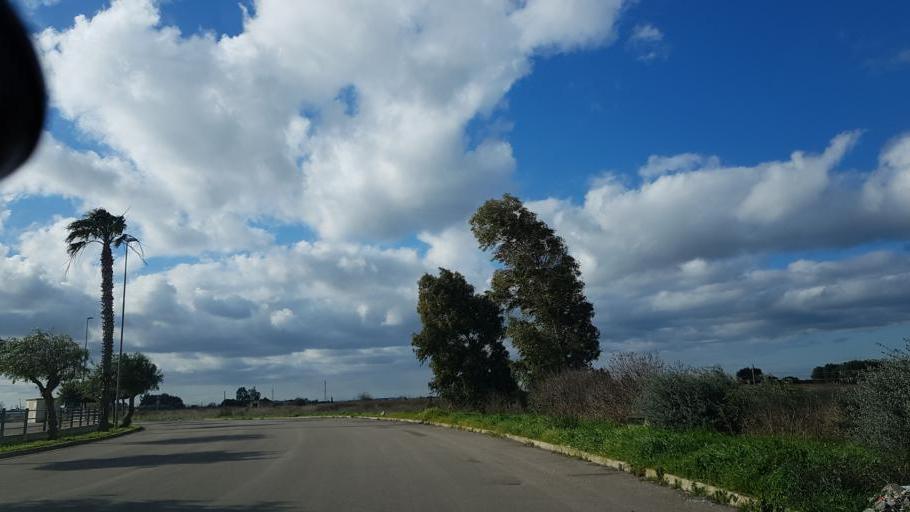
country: IT
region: Apulia
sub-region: Provincia di Brindisi
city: Brindisi
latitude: 40.6196
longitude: 17.9009
